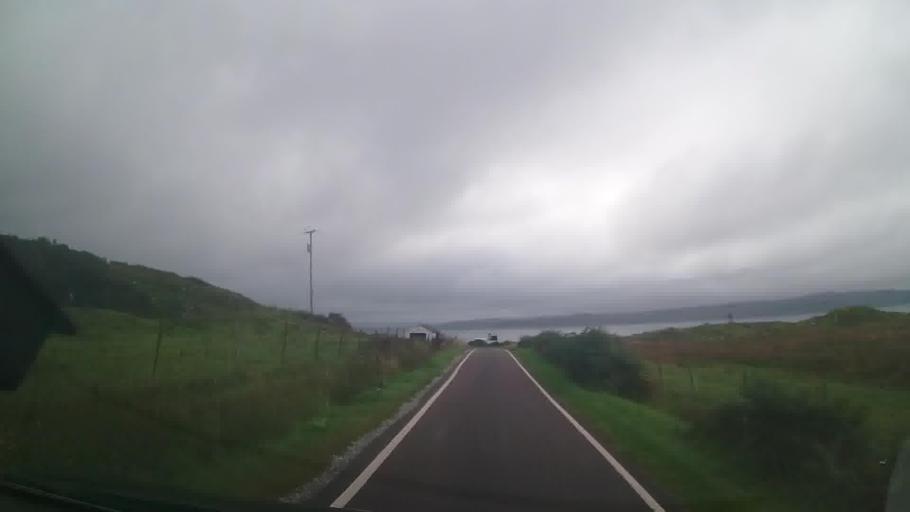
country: GB
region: Scotland
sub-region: Argyll and Bute
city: Isle Of Mull
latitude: 56.6924
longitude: -6.0946
